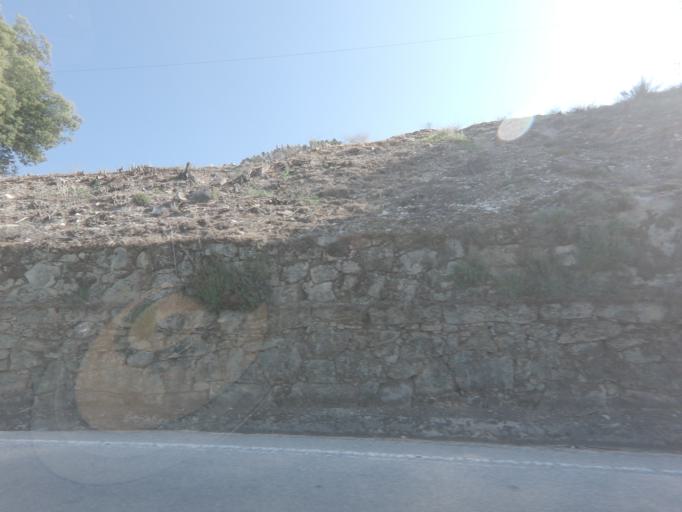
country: PT
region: Viseu
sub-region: Tabuaco
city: Tabuaco
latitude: 41.1149
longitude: -7.5710
